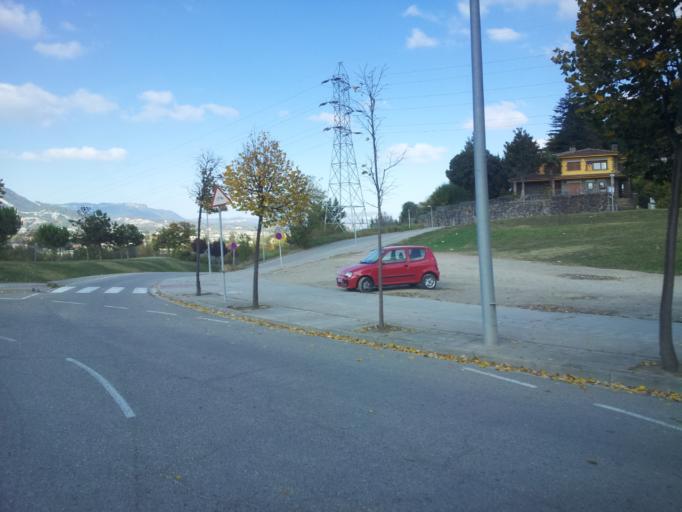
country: ES
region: Catalonia
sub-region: Provincia de Barcelona
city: Vic
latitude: 41.9336
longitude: 2.2450
